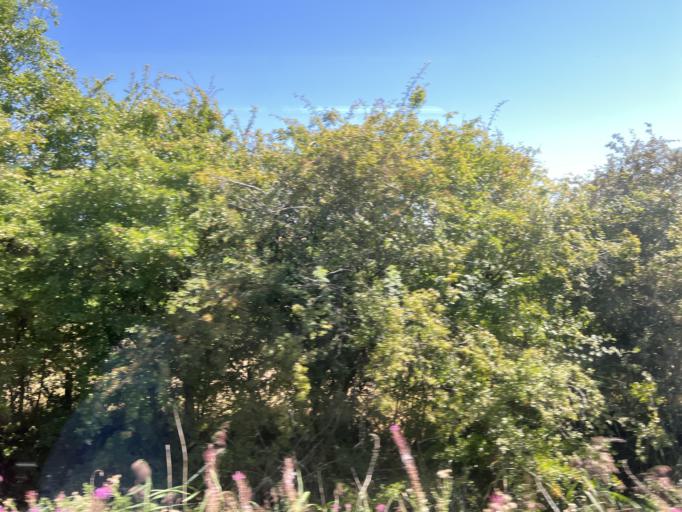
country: GB
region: England
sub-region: Lincolnshire
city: Spilsby
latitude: 53.1372
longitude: 0.1582
